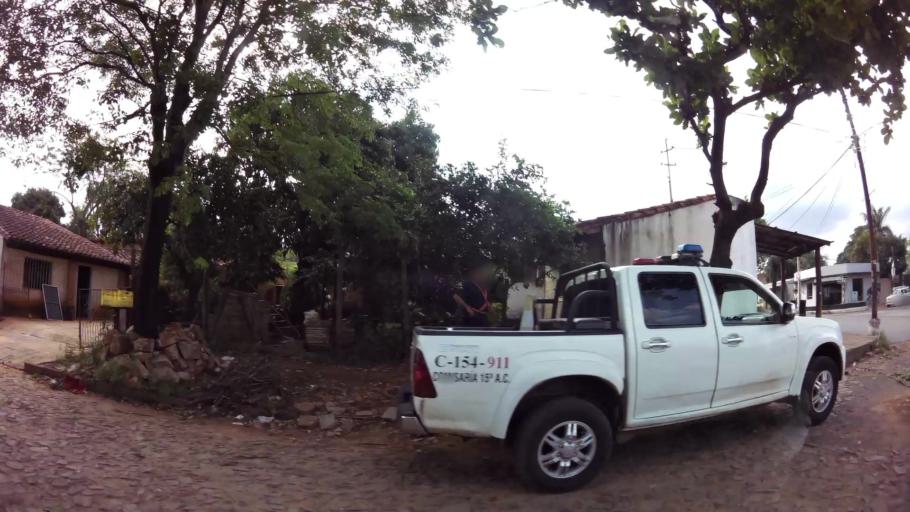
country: PY
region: Central
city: Fernando de la Mora
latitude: -25.3467
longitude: -57.5433
